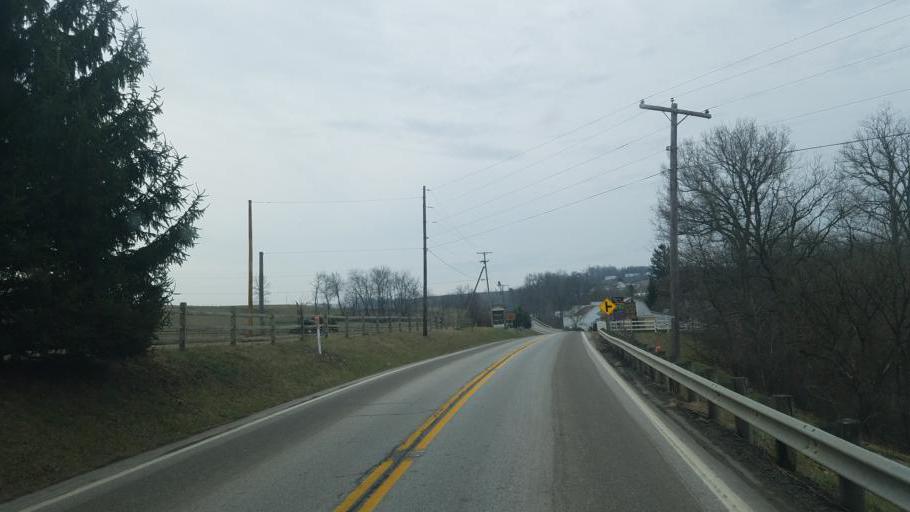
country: US
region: Ohio
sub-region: Holmes County
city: Millersburg
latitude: 40.5231
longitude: -81.8040
